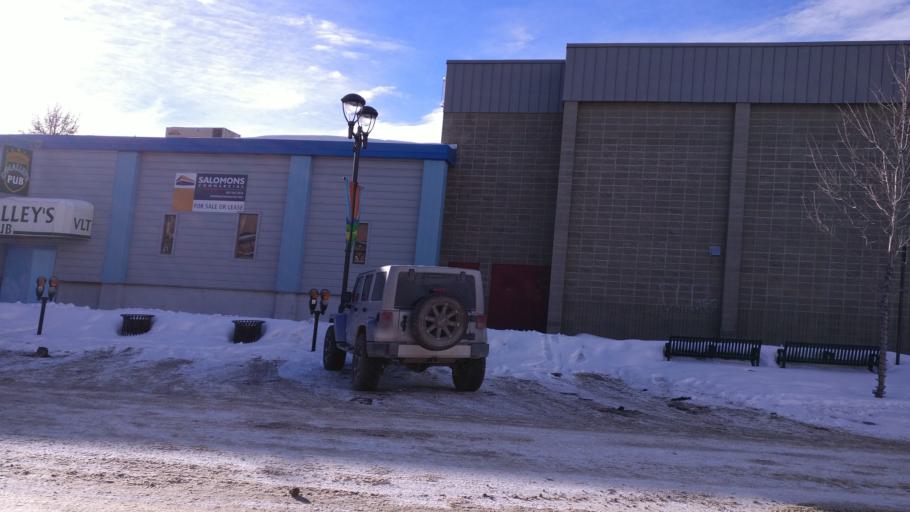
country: CA
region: Alberta
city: Red Deer
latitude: 52.2658
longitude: -113.8140
